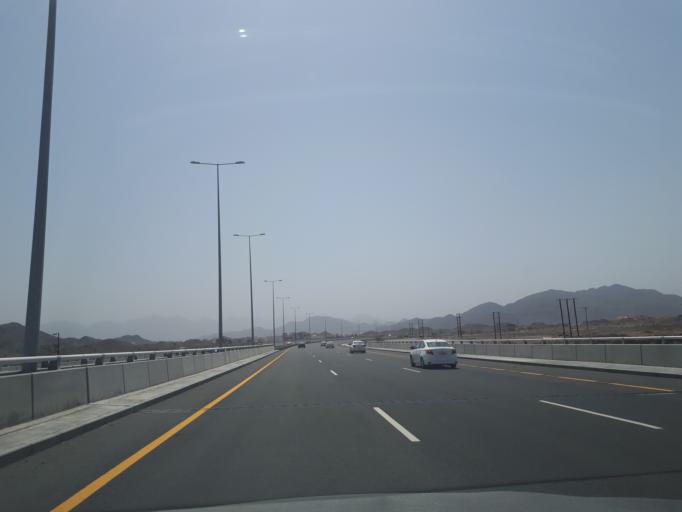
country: OM
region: Muhafazat ad Dakhiliyah
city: Bidbid
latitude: 23.3437
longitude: 58.1022
